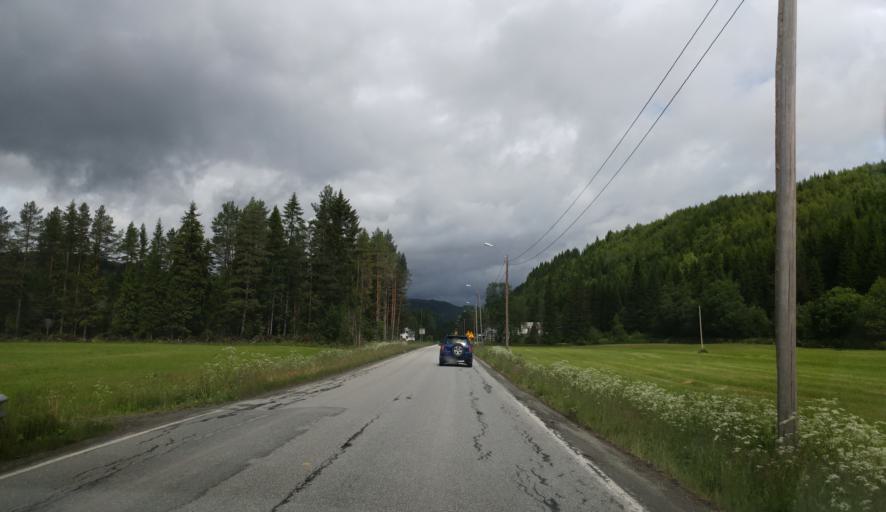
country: NO
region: Sor-Trondelag
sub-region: Selbu
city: Mebonden
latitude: 63.2796
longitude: 11.0807
